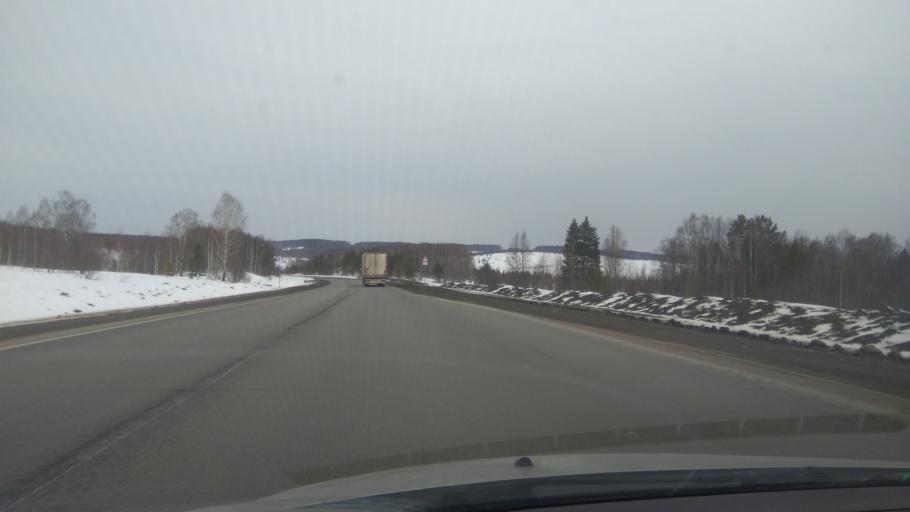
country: RU
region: Sverdlovsk
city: Ufimskiy
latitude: 56.7884
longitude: 58.3571
